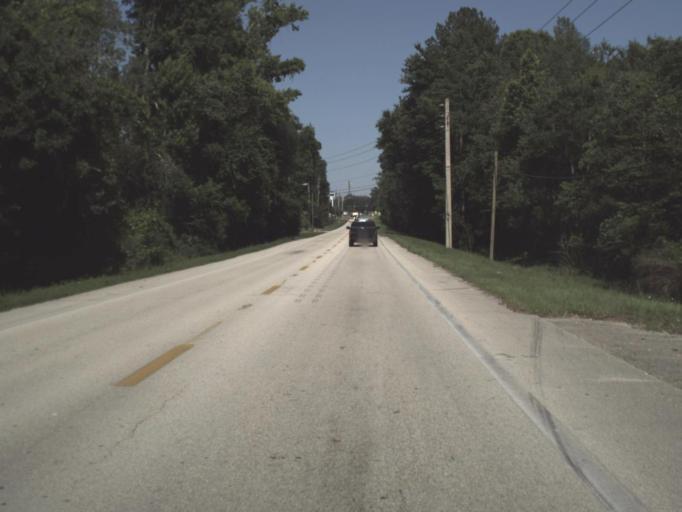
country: US
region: Florida
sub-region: Duval County
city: Baldwin
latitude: 30.3136
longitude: -81.8544
